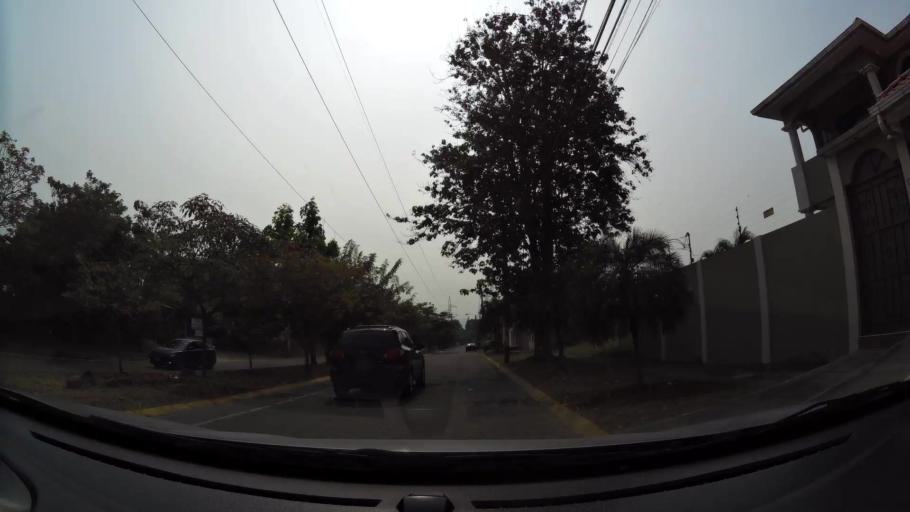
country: HN
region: Cortes
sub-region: San Pedro Sula
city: Pena Blanca
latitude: 15.5381
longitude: -88.0307
